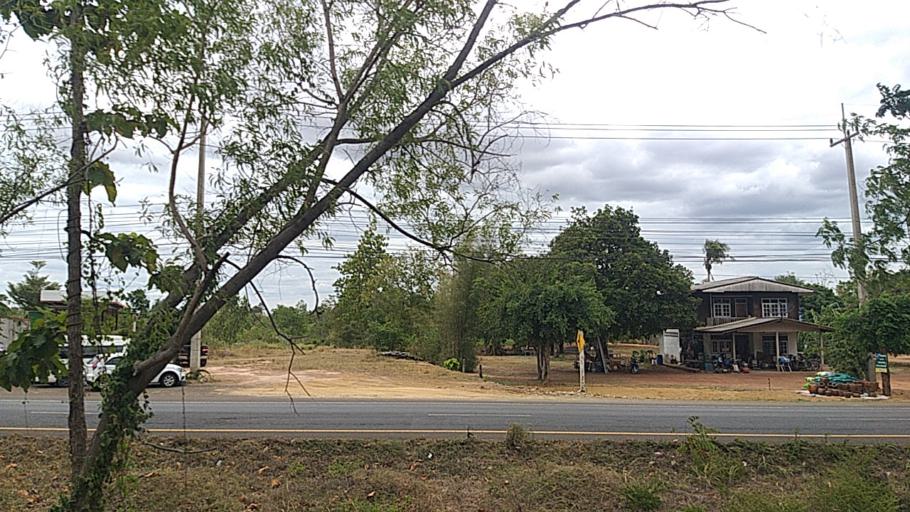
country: TH
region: Buriram
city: Non Suwan
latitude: 14.6448
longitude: 102.6774
